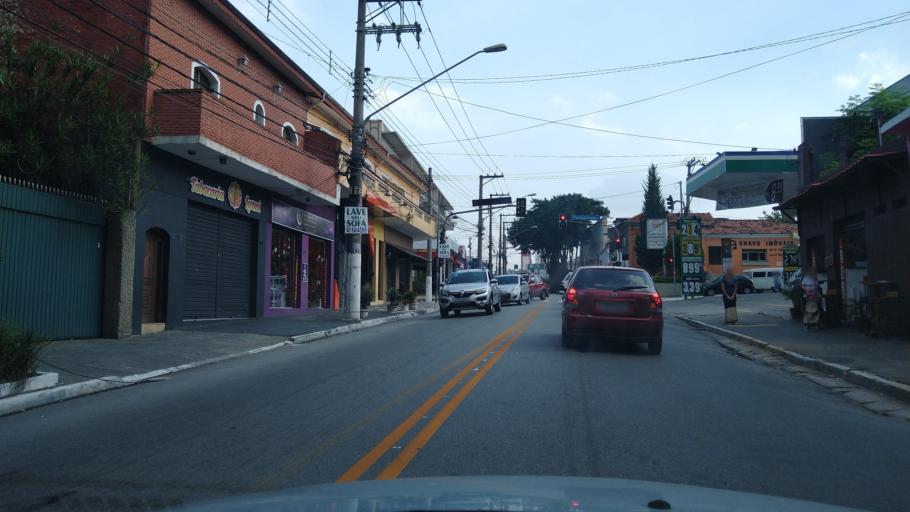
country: BR
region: Sao Paulo
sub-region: Guarulhos
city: Guarulhos
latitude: -23.4715
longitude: -46.5869
